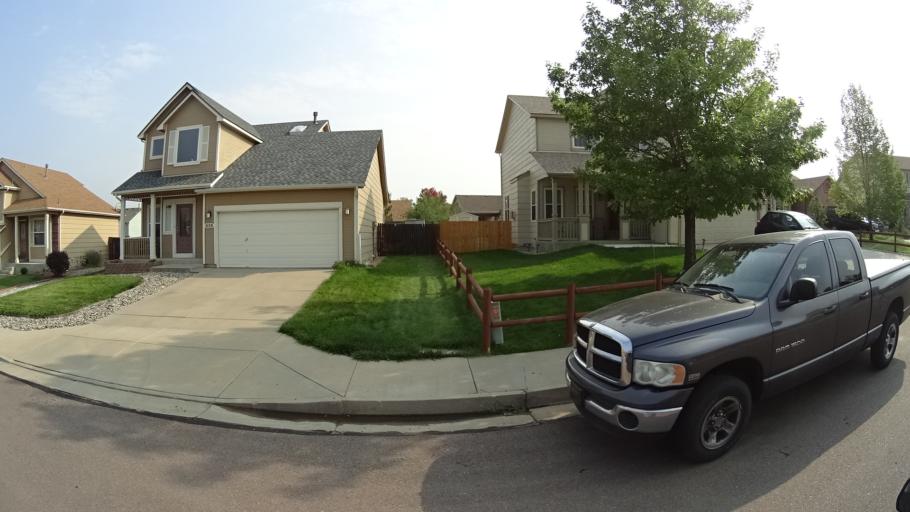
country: US
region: Colorado
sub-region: El Paso County
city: Stratmoor
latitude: 38.8197
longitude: -104.7510
